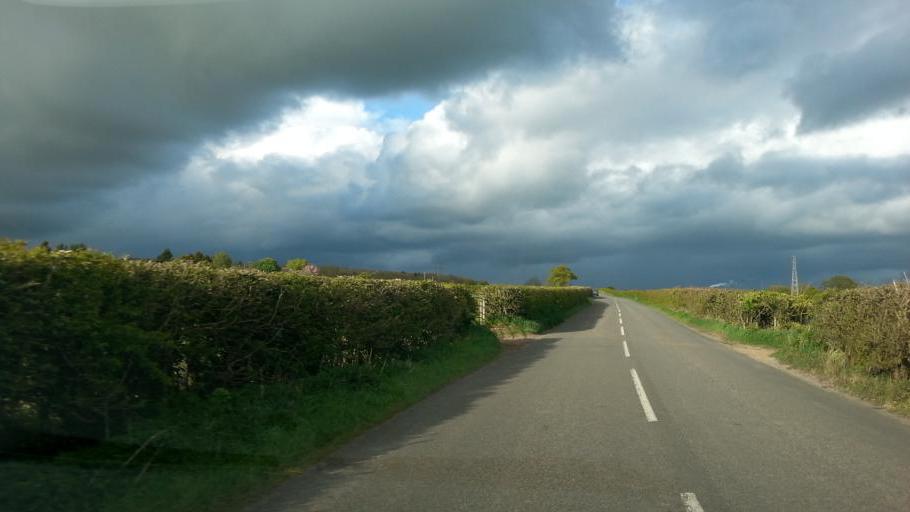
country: GB
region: England
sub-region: Nottinghamshire
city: Southwell
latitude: 53.1078
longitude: -0.9236
